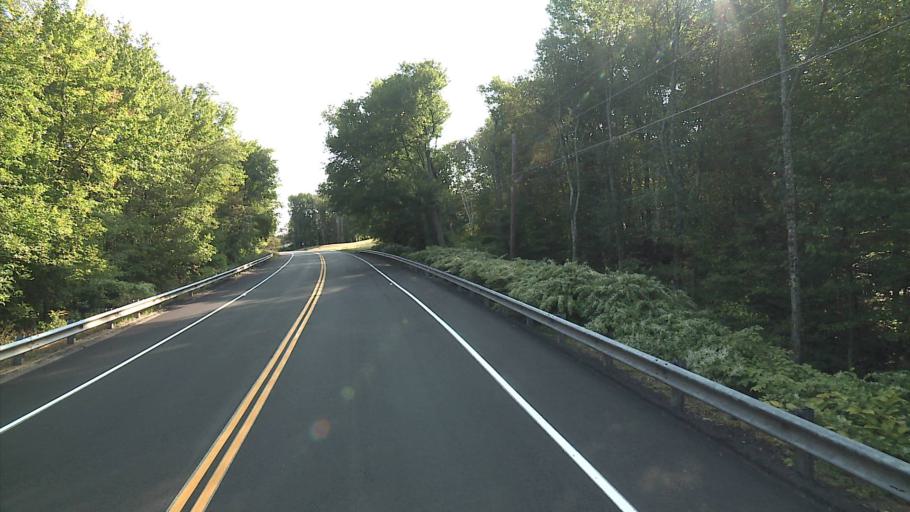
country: US
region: Connecticut
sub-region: Tolland County
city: Hebron
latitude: 41.7247
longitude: -72.3962
